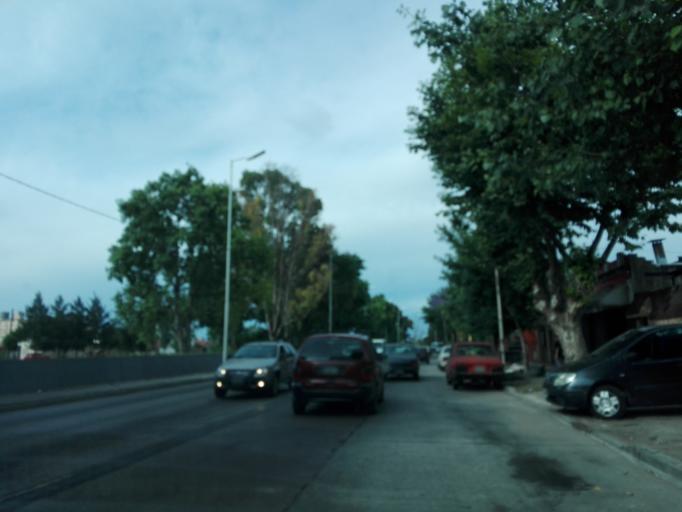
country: AR
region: Buenos Aires
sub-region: Partido de Avellaneda
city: Avellaneda
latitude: -34.6798
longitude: -58.3393
